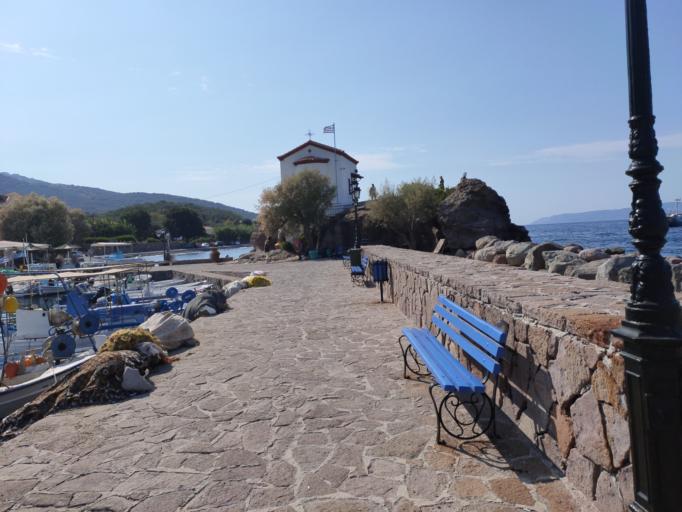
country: GR
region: North Aegean
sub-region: Nomos Lesvou
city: Mantamados
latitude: 39.3741
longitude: 26.3035
